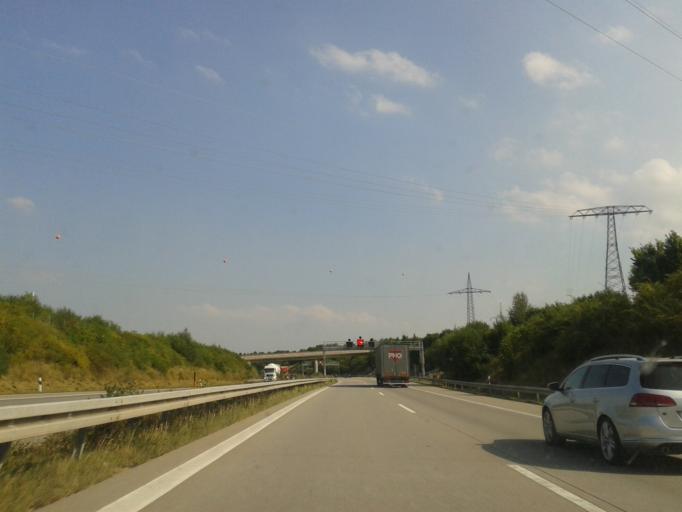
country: DE
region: Saxony
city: Freital
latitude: 51.0324
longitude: 13.6686
